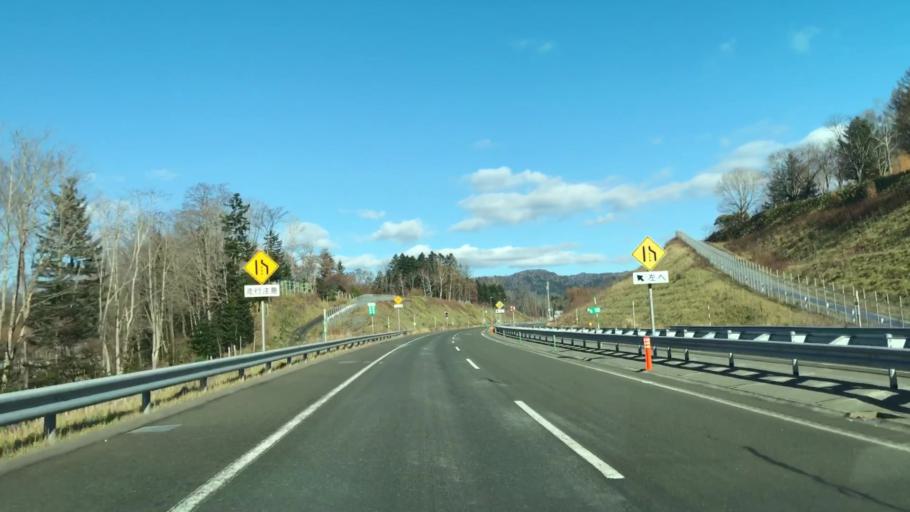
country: JP
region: Hokkaido
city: Shimo-furano
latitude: 42.9383
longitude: 142.2096
